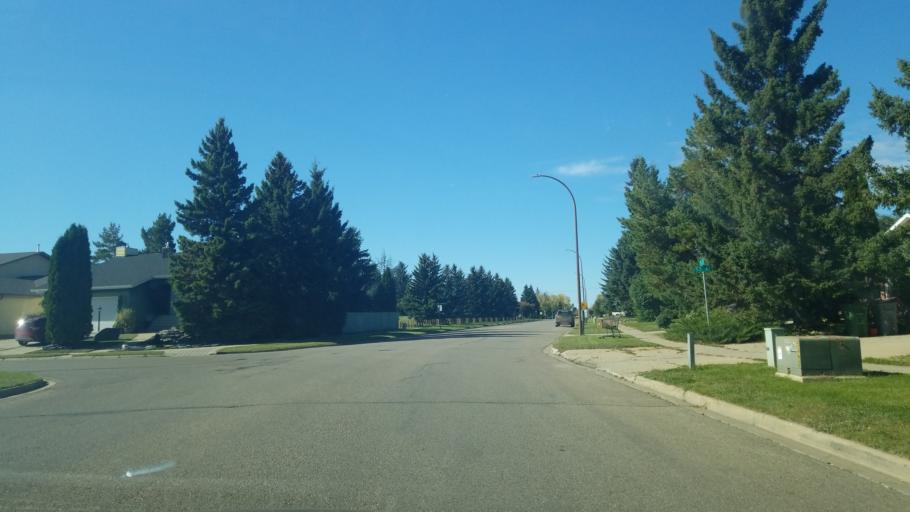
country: CA
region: Saskatchewan
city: Lloydminster
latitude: 53.2730
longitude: -110.0143
